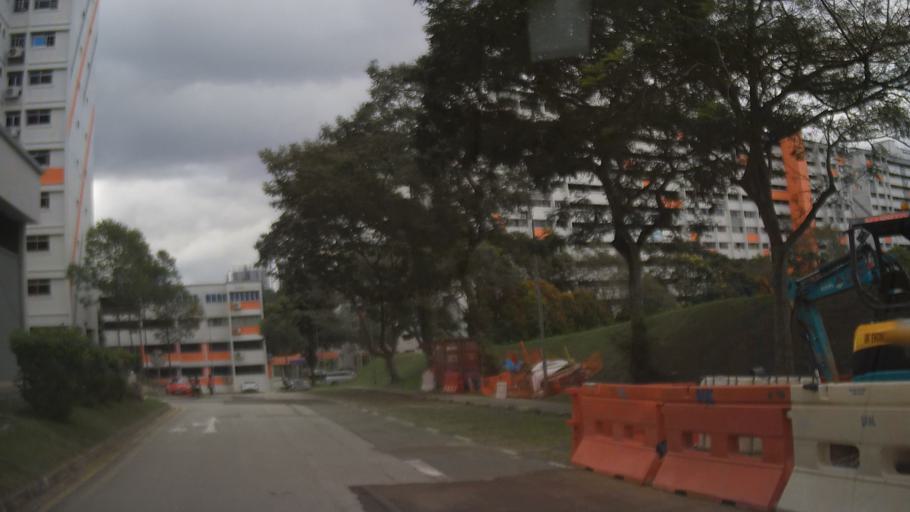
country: MY
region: Johor
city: Johor Bahru
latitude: 1.4316
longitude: 103.7818
